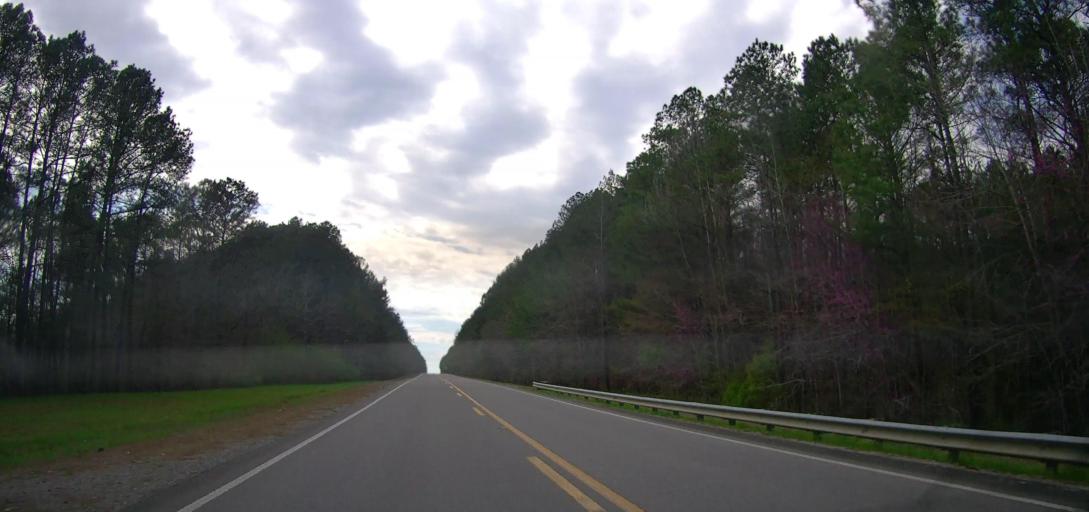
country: US
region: Alabama
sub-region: Marion County
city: Winfield
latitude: 33.9332
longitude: -87.7379
